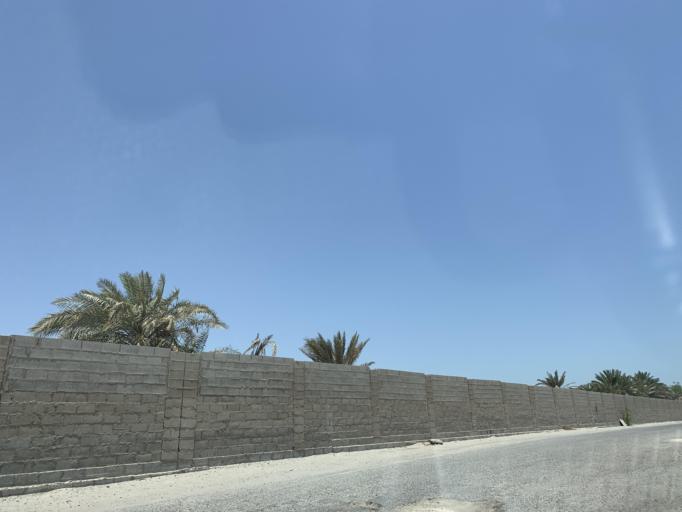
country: BH
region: Manama
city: Jidd Hafs
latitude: 26.2215
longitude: 50.4821
